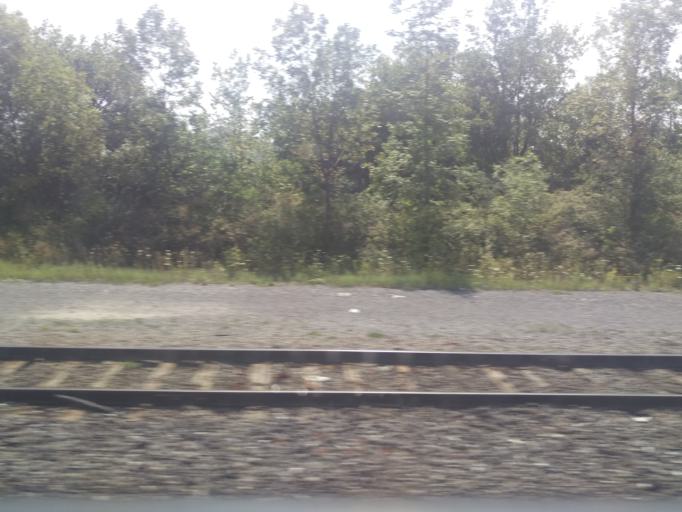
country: CA
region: Ontario
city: Kingston
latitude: 44.2654
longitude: -76.5117
